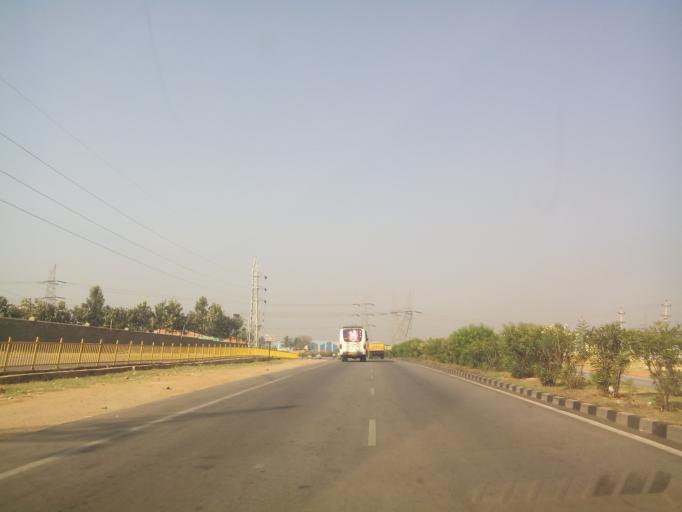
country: IN
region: Karnataka
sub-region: Bangalore Rural
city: Nelamangala
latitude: 13.0950
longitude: 77.3807
